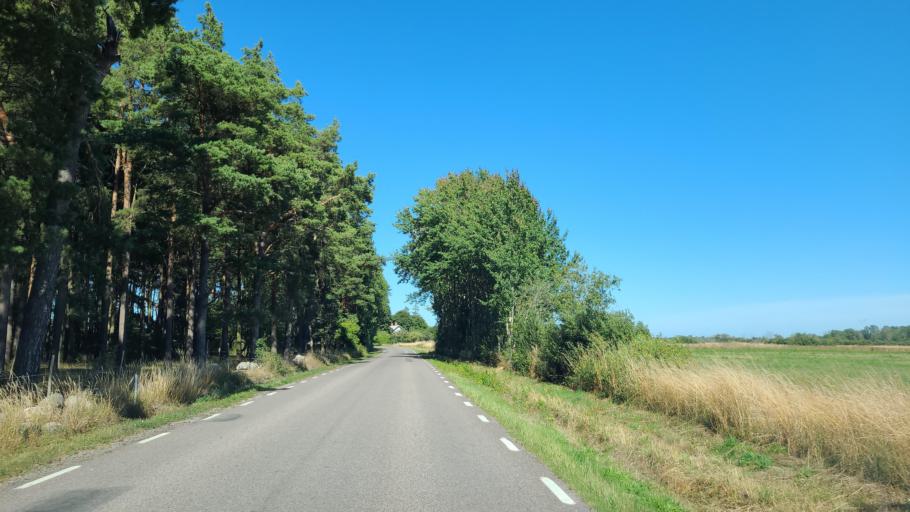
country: SE
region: Kalmar
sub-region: Borgholms Kommun
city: Borgholm
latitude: 56.8504
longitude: 16.8023
